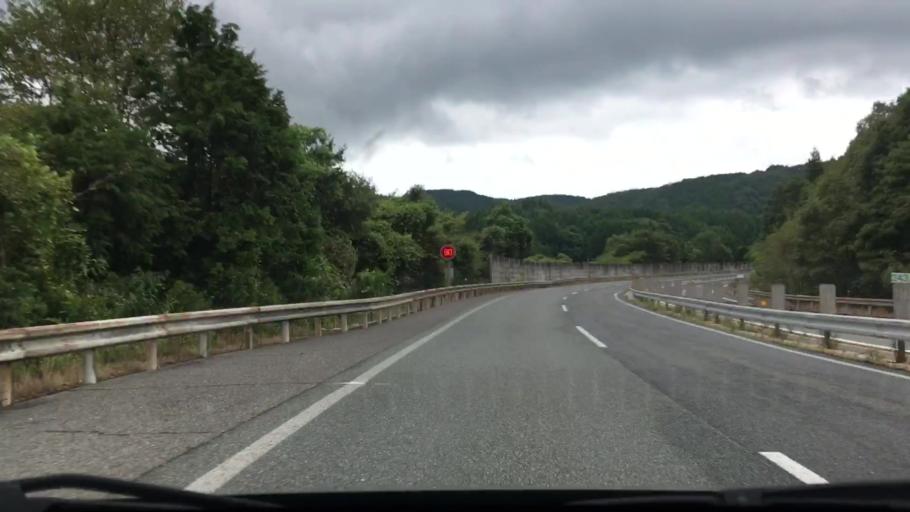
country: JP
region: Okayama
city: Niimi
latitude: 34.9056
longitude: 133.3020
